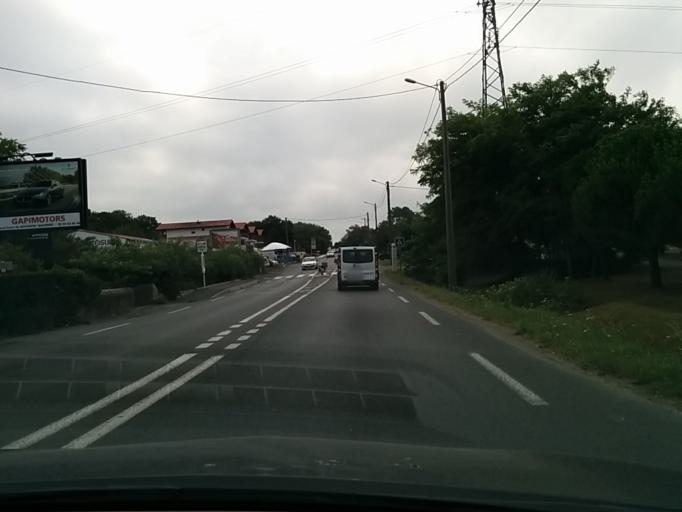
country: FR
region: Aquitaine
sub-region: Departement des Pyrenees-Atlantiques
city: Arbonne
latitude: 43.4508
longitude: -1.5654
